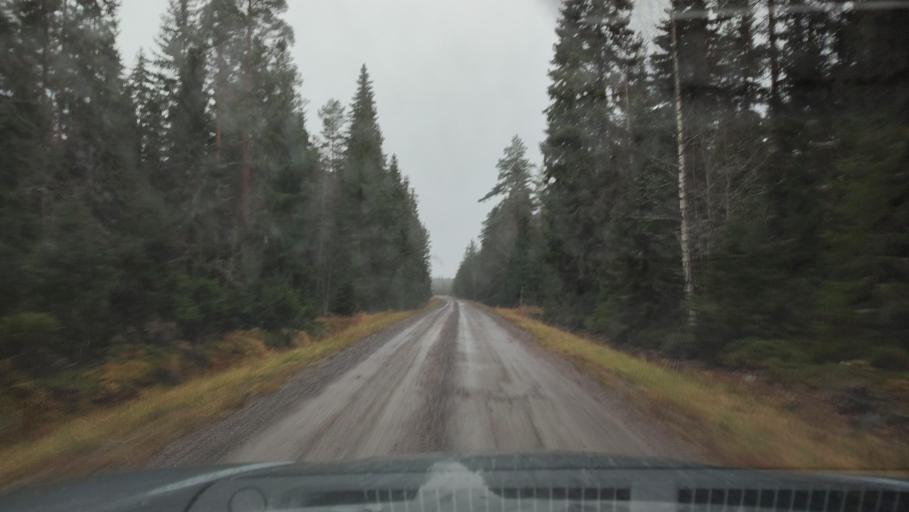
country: FI
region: Southern Ostrobothnia
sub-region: Suupohja
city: Karijoki
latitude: 62.2205
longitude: 21.7430
